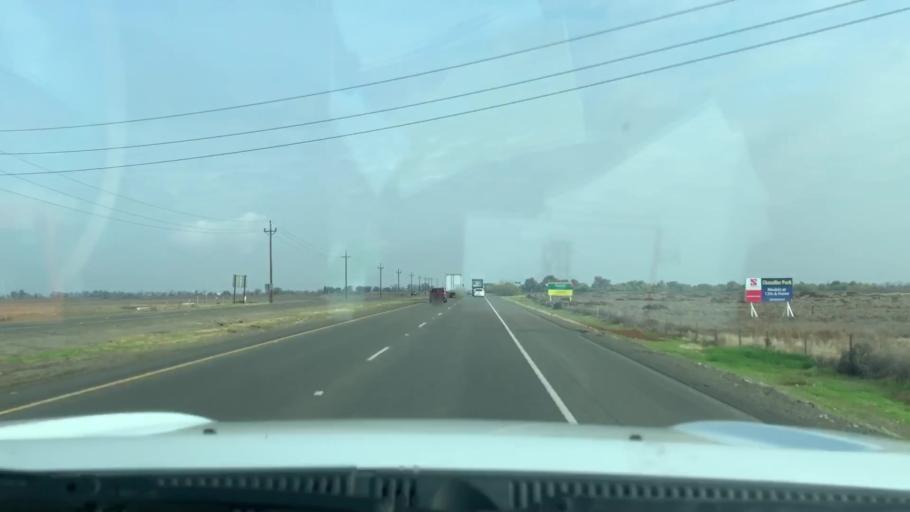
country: US
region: California
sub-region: Kings County
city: Lemoore Station
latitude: 36.2570
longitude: -119.8653
